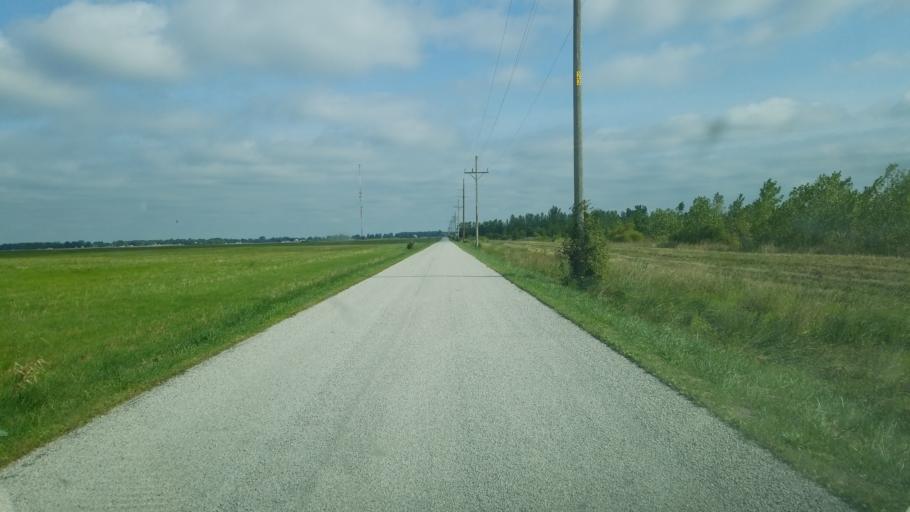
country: US
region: Ohio
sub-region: Marion County
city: Marion
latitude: 40.5880
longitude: -83.2033
